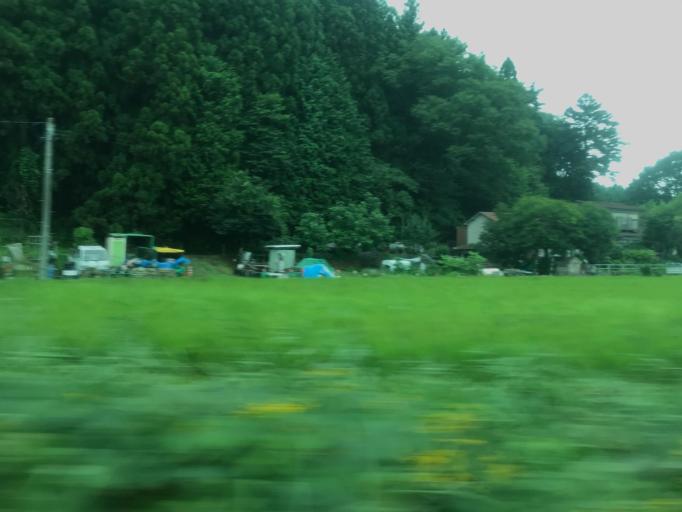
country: JP
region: Fukushima
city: Ishikawa
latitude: 37.1289
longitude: 140.2455
